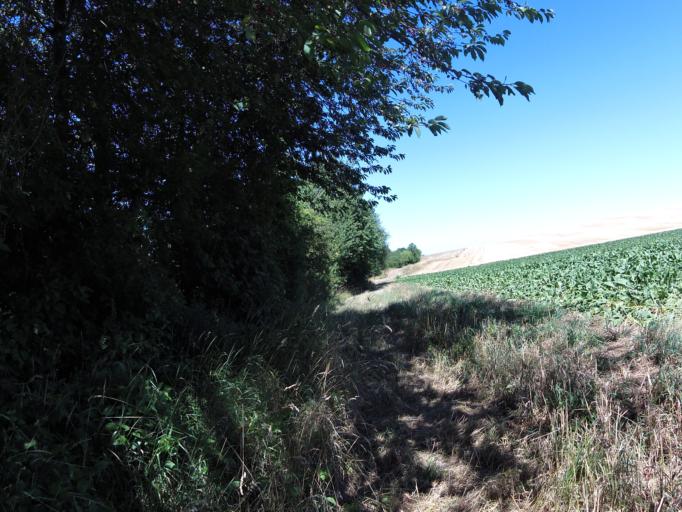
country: DE
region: Bavaria
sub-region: Regierungsbezirk Unterfranken
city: Gerbrunn
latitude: 49.7662
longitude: 10.0005
